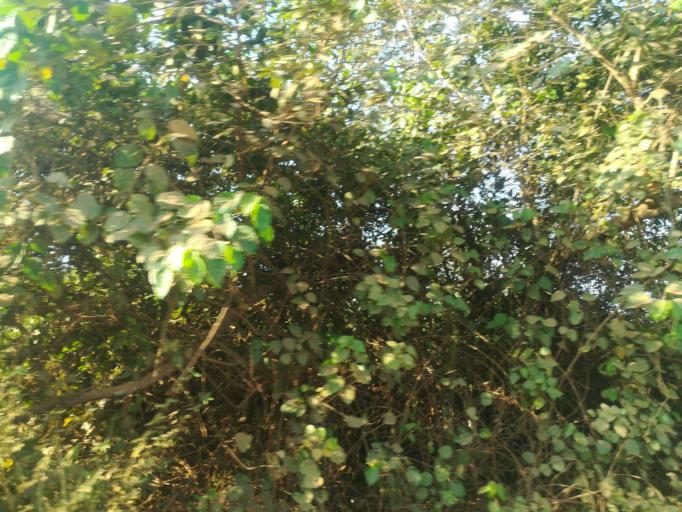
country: NG
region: Ogun
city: Ayetoro
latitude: 7.2130
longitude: 3.1883
